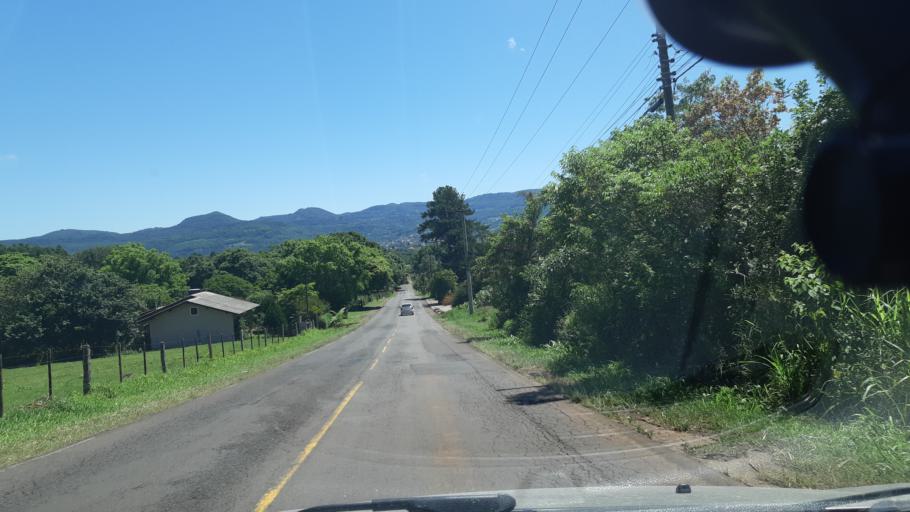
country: BR
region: Rio Grande do Sul
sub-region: Novo Hamburgo
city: Novo Hamburgo
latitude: -29.6181
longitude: -51.0927
